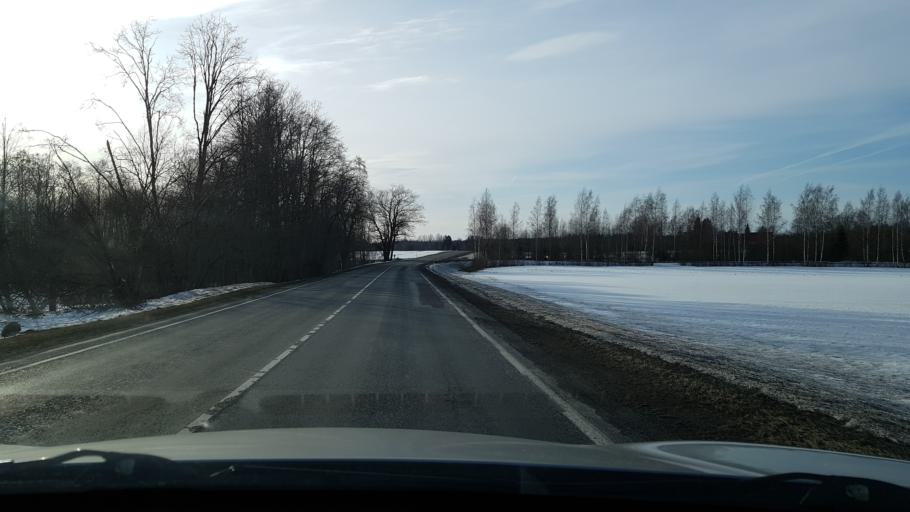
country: EE
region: Viljandimaa
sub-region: Suure-Jaani vald
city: Suure-Jaani
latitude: 58.3530
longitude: 25.3853
